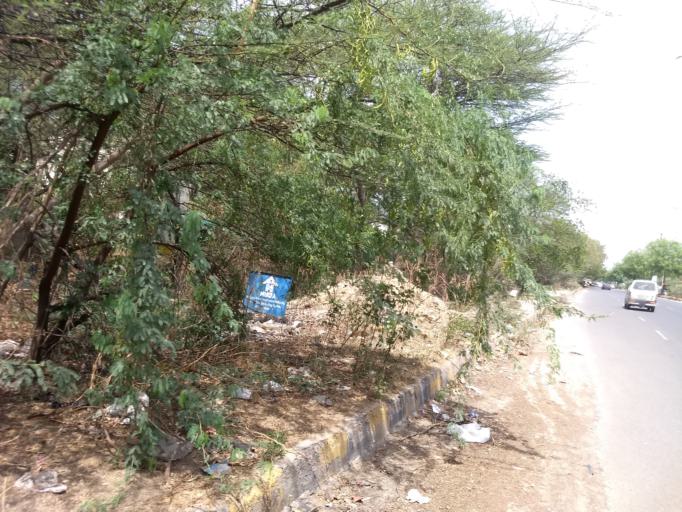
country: IN
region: Haryana
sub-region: Gurgaon
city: Gurgaon
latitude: 28.4638
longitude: 77.0999
